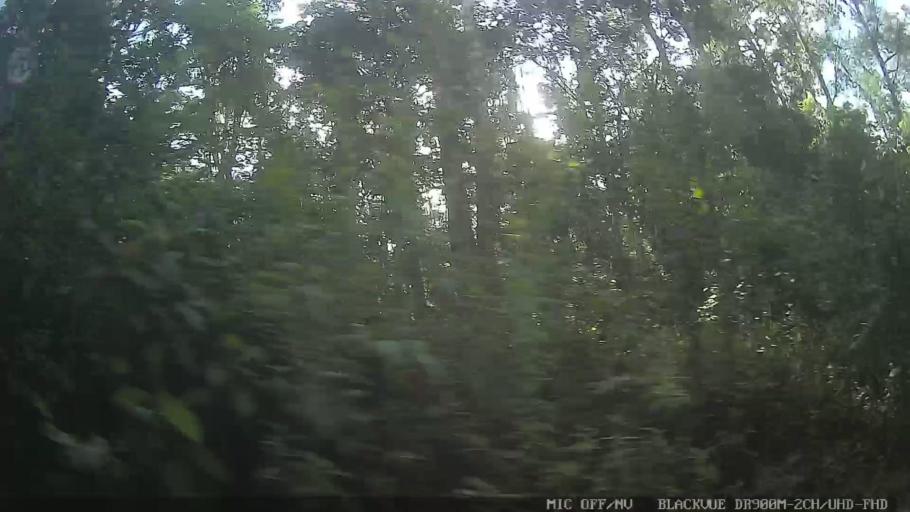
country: BR
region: Sao Paulo
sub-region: Bom Jesus Dos Perdoes
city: Bom Jesus dos Perdoes
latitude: -23.1582
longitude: -46.5113
